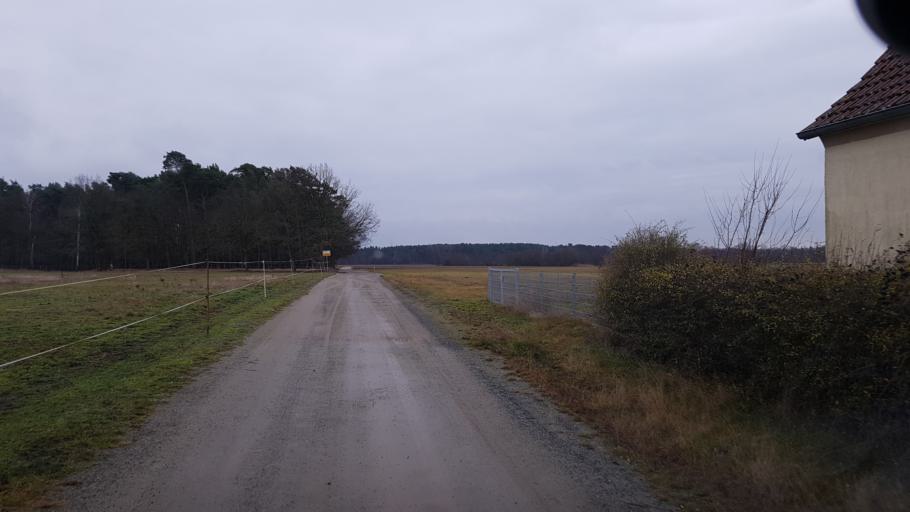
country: DE
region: Brandenburg
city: Altdobern
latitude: 51.6917
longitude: 14.0439
